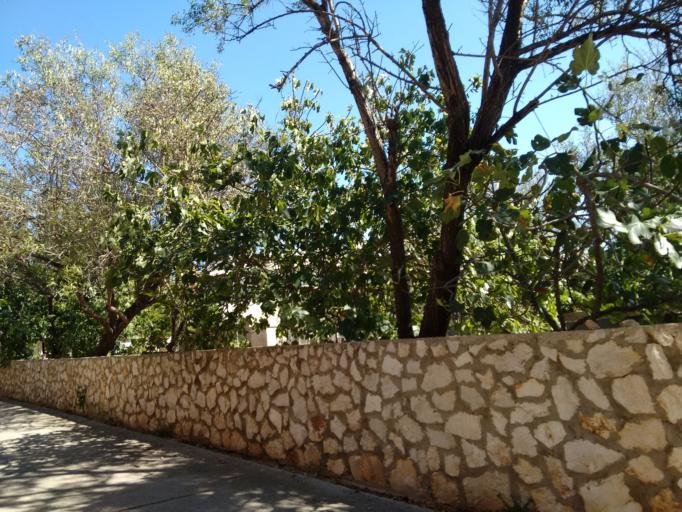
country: HR
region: Licko-Senjska
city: Novalja
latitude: 44.3746
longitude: 14.6960
